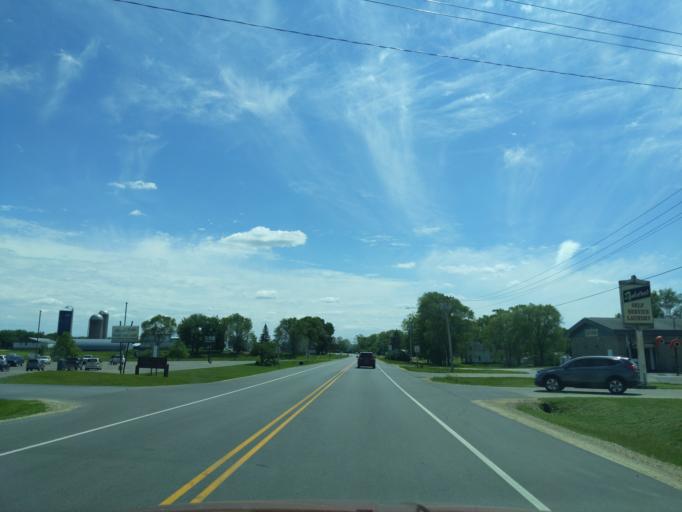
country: US
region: Wisconsin
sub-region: Columbia County
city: Pardeeville
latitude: 43.5261
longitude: -89.3040
